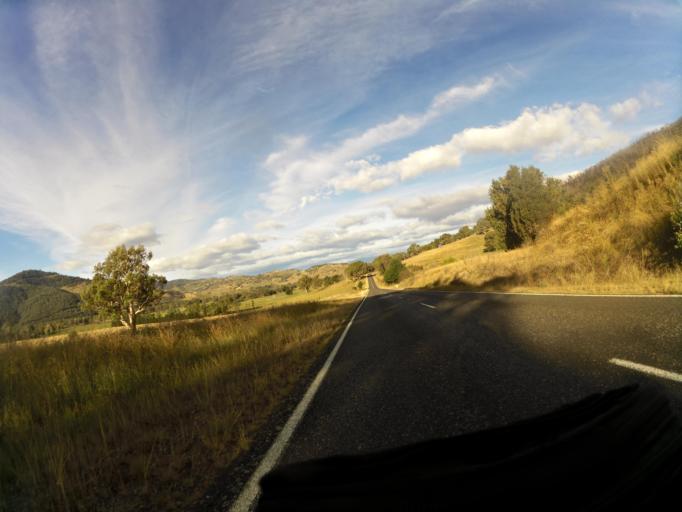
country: AU
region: New South Wales
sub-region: Greater Hume Shire
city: Holbrook
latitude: -36.0064
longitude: 147.8919
